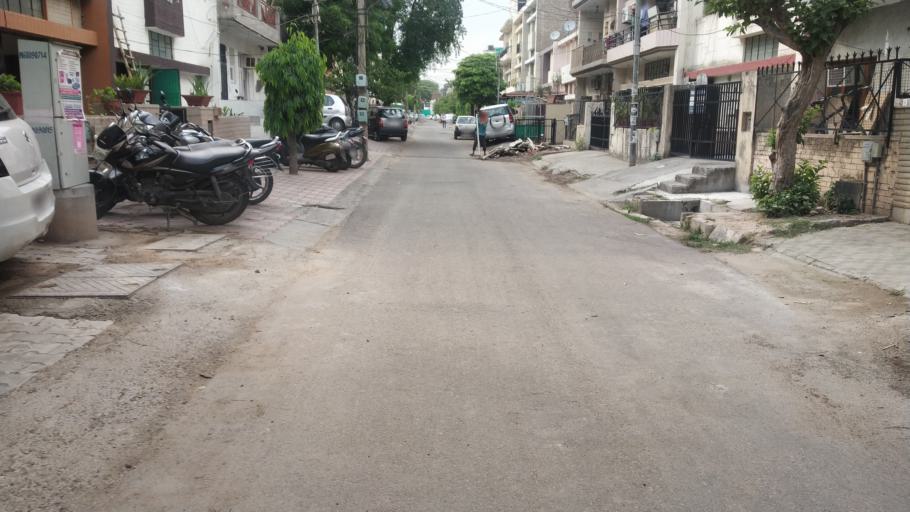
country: IN
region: Punjab
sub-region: Ajitgarh
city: Mohali
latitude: 30.7054
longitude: 76.7178
